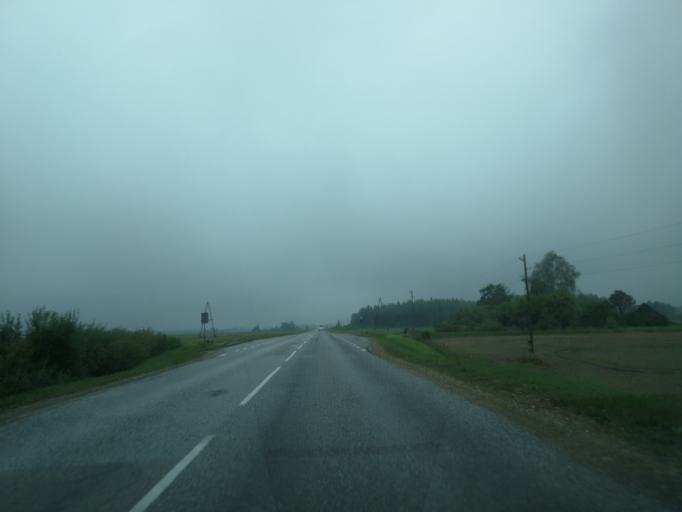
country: LV
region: Preilu Rajons
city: Preili
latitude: 56.3065
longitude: 26.6017
